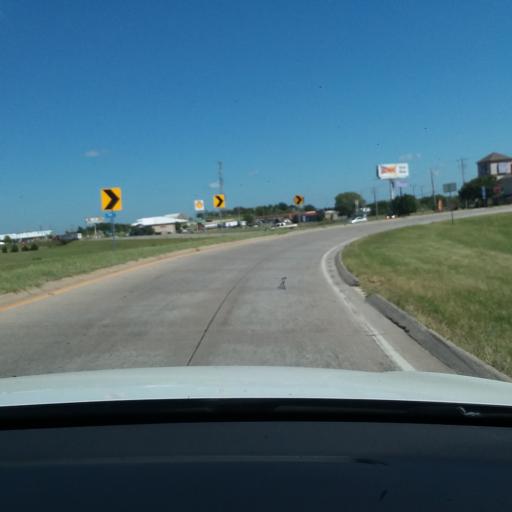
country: US
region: Oklahoma
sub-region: Oklahoma County
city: Edmond
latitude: 35.5919
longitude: -97.4337
